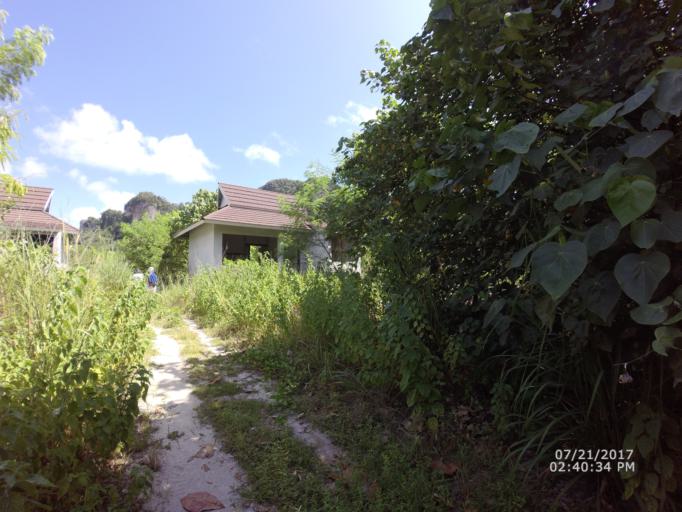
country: TH
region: Phangnga
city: Ban Phru Nai
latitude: 7.7627
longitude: 98.7654
